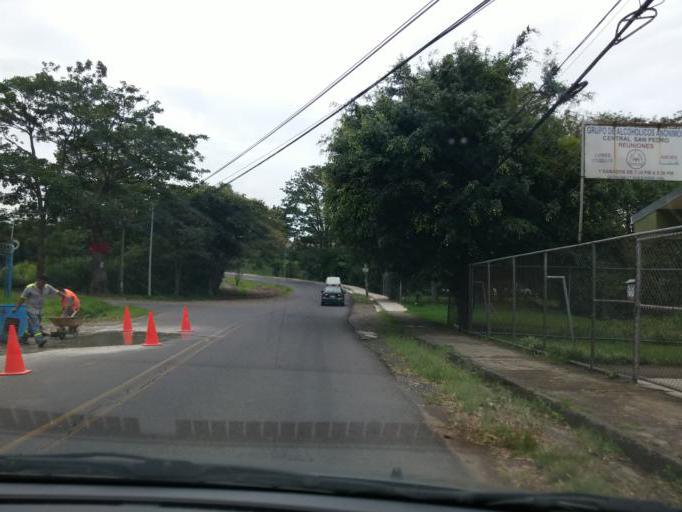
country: CR
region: San Jose
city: San Pedro
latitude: 9.9286
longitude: -84.0452
